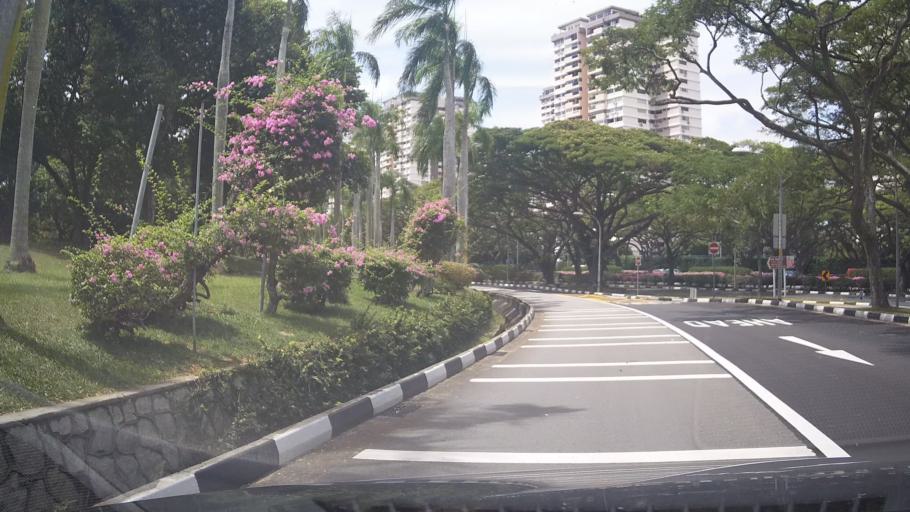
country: SG
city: Singapore
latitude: 1.3077
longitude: 103.9337
